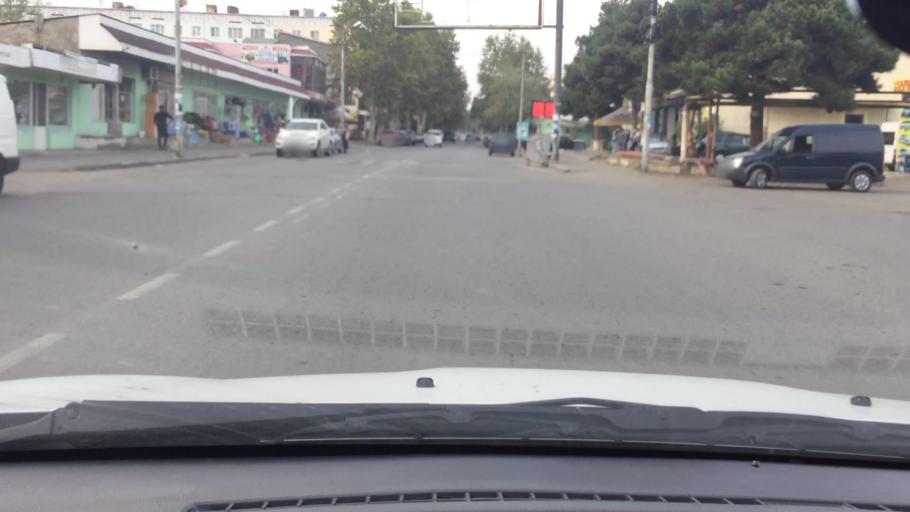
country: GE
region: Kvemo Kartli
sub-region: Marneuli
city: Marneuli
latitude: 41.4682
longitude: 44.8179
